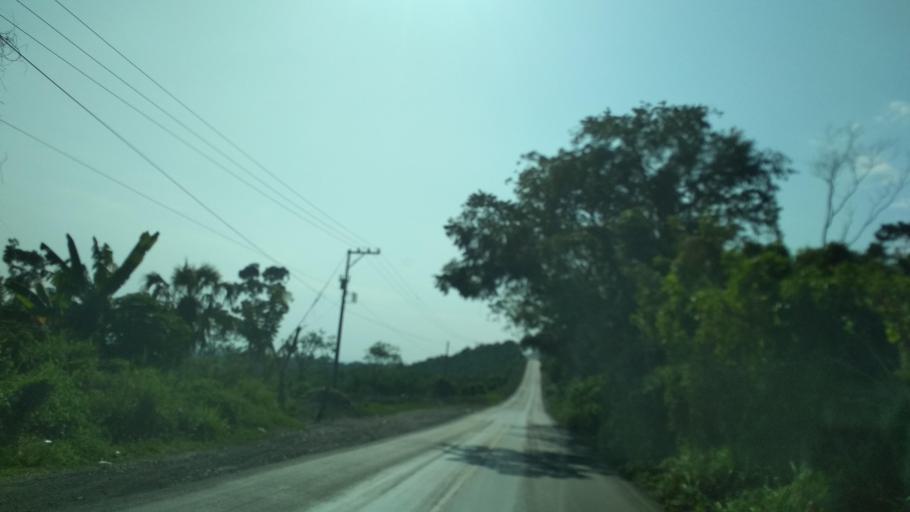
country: MX
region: Veracruz
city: Agua Dulce
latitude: 20.3986
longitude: -97.2631
